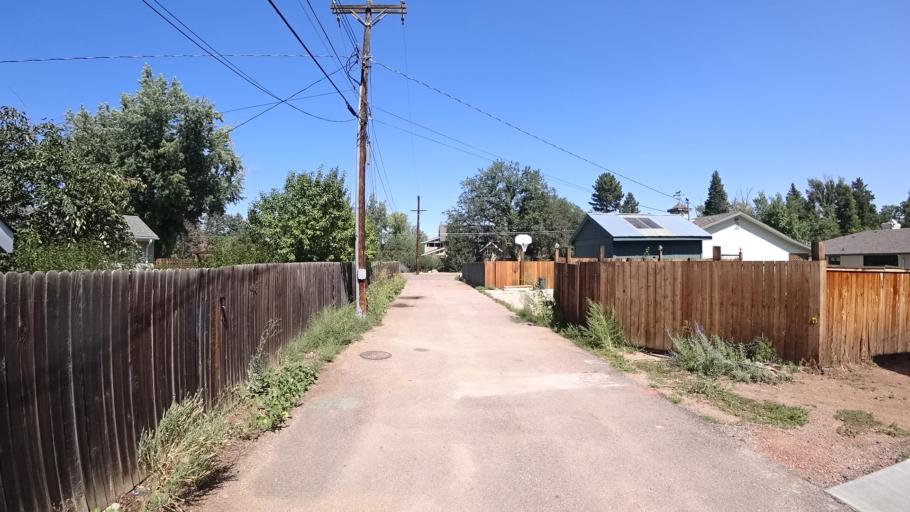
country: US
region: Colorado
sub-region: El Paso County
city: Colorado Springs
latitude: 38.8575
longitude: -104.8299
